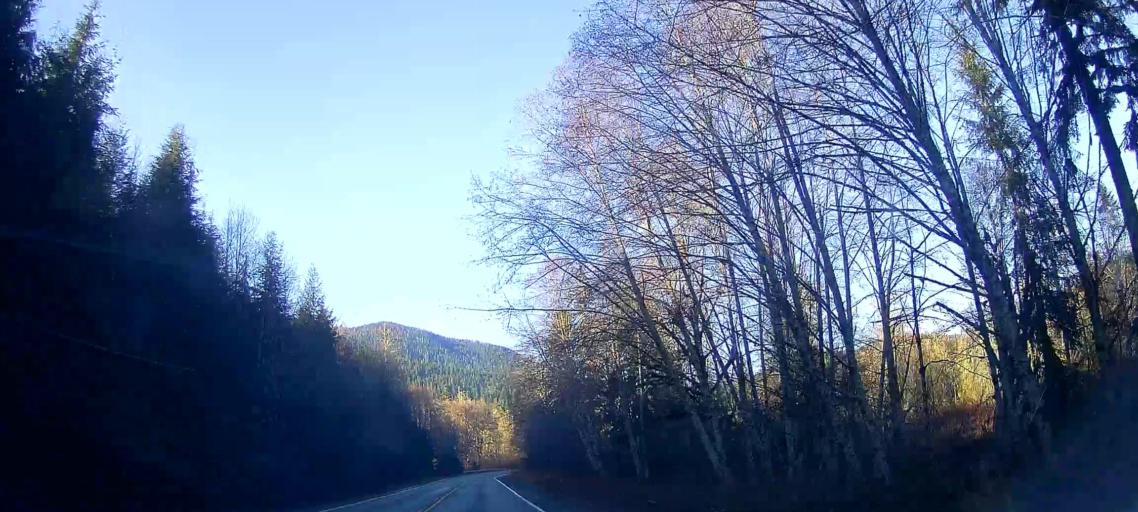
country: US
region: Washington
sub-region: Snohomish County
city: Darrington
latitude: 48.6320
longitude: -121.7397
